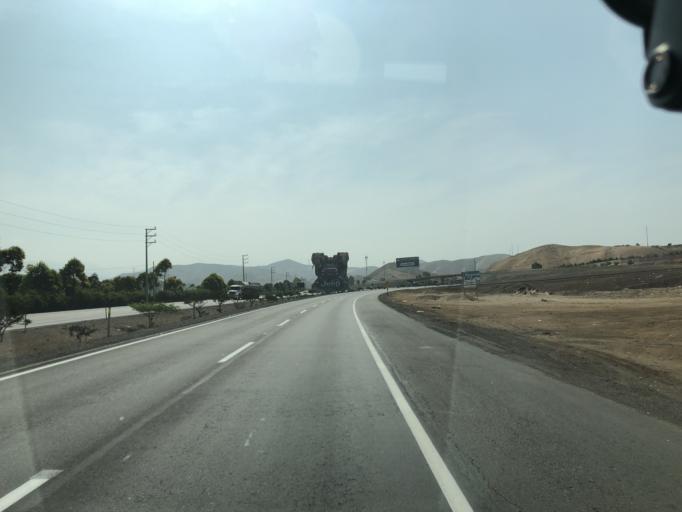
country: PE
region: Lima
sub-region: Provincia de Canete
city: Mala
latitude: -12.5857
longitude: -76.6677
